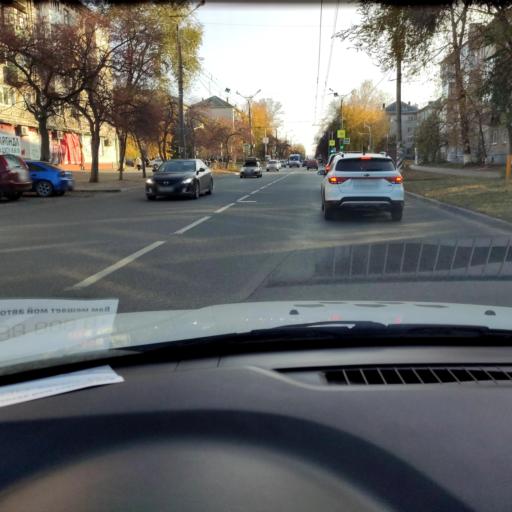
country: RU
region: Samara
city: Tol'yatti
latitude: 53.5173
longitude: 49.4164
